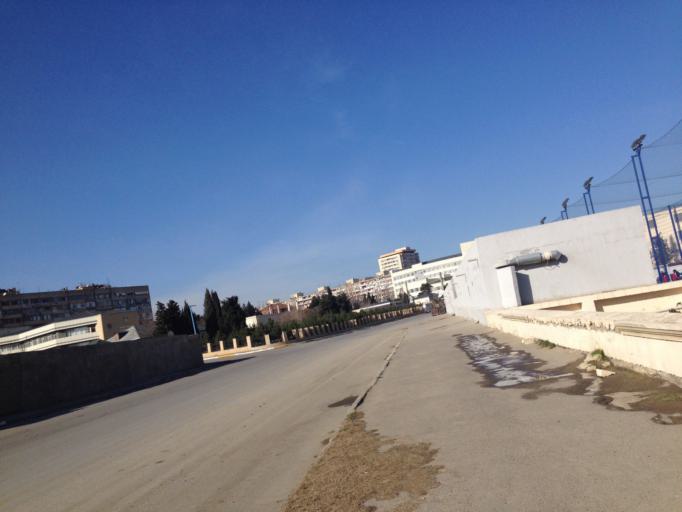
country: AZ
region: Baki
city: Baku
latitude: 40.4107
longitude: 49.8536
